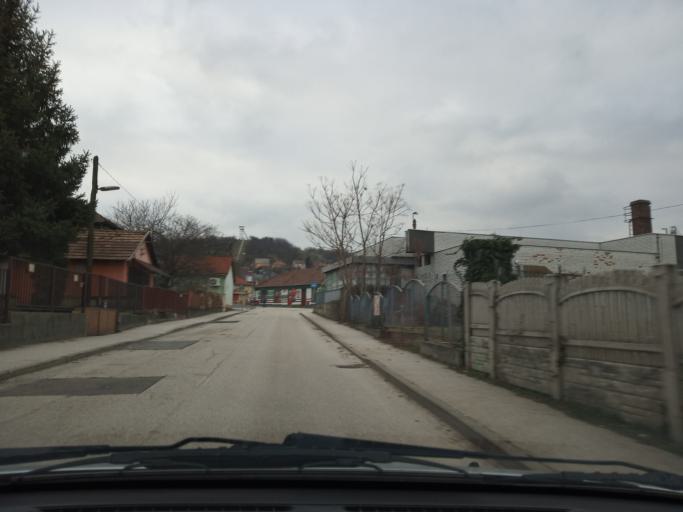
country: HU
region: Komarom-Esztergom
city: Dorog
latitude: 47.7216
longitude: 18.7300
